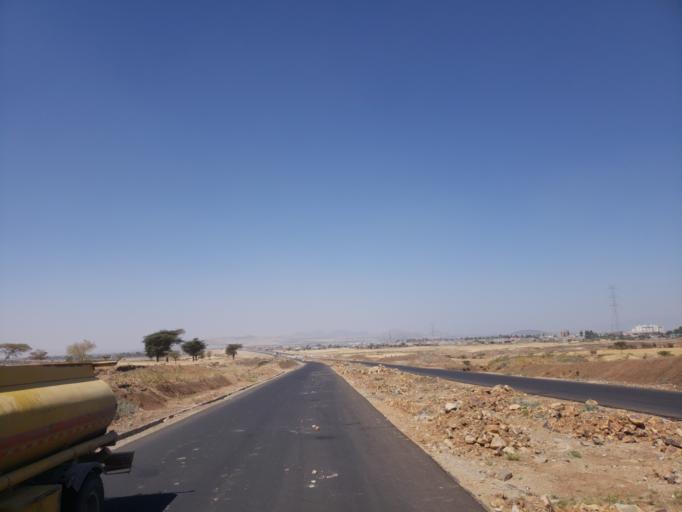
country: ET
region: Oromiya
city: Mojo
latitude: 8.5664
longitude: 39.1517
